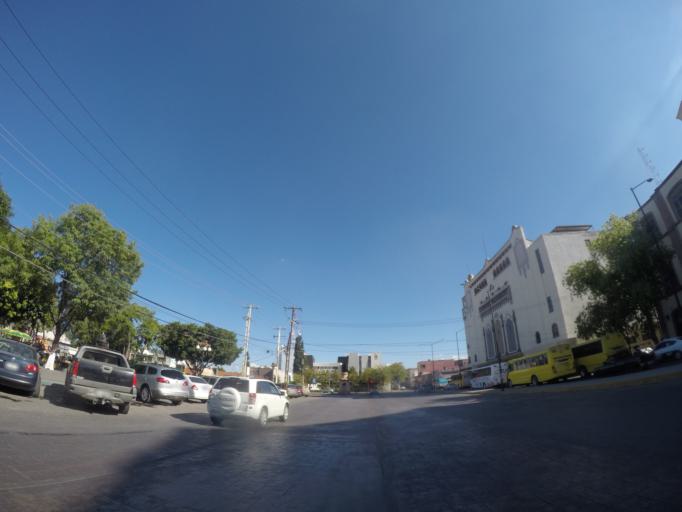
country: MX
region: San Luis Potosi
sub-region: San Luis Potosi
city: San Luis Potosi
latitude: 22.1511
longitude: -100.9727
